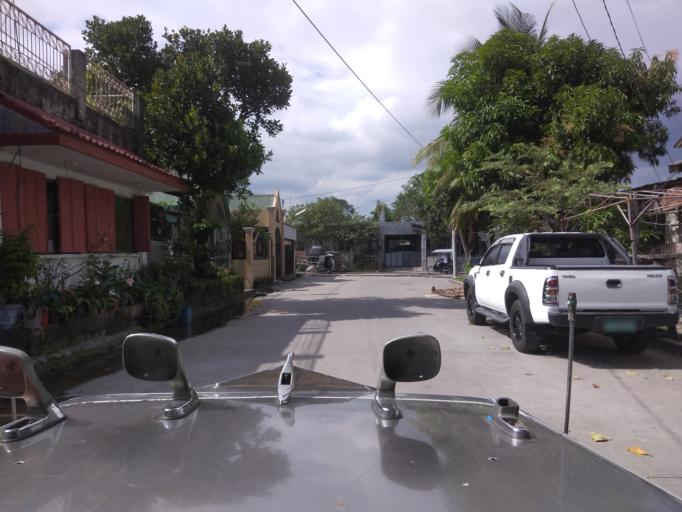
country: PH
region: Central Luzon
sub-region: Province of Pampanga
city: Pandacaqui
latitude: 15.1809
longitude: 120.6417
